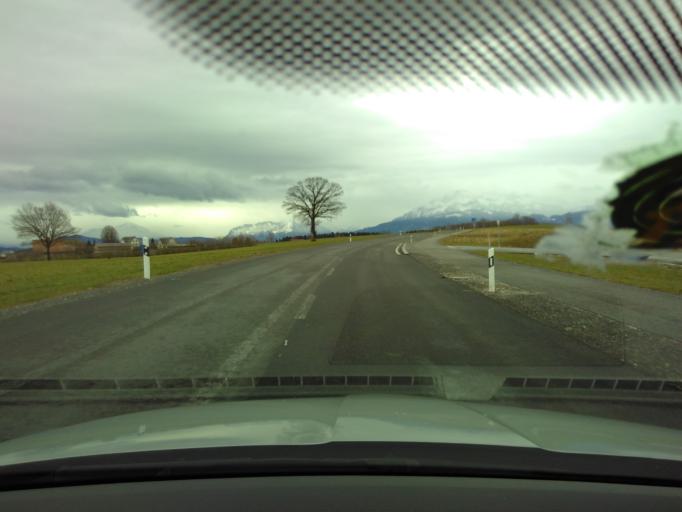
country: CH
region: Lucerne
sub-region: Sursee District
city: Hildisrieden
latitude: 47.1325
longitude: 8.2415
